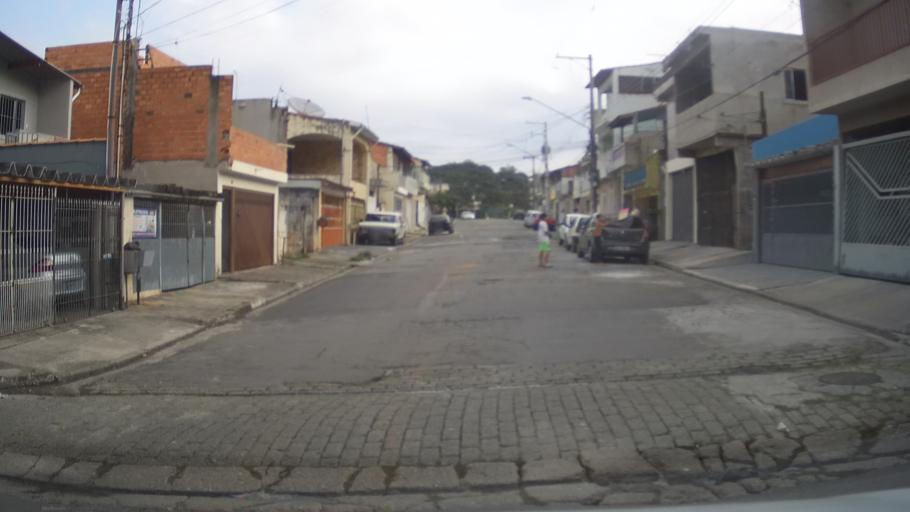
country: BR
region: Sao Paulo
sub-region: Guarulhos
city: Guarulhos
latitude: -23.4143
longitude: -46.5107
